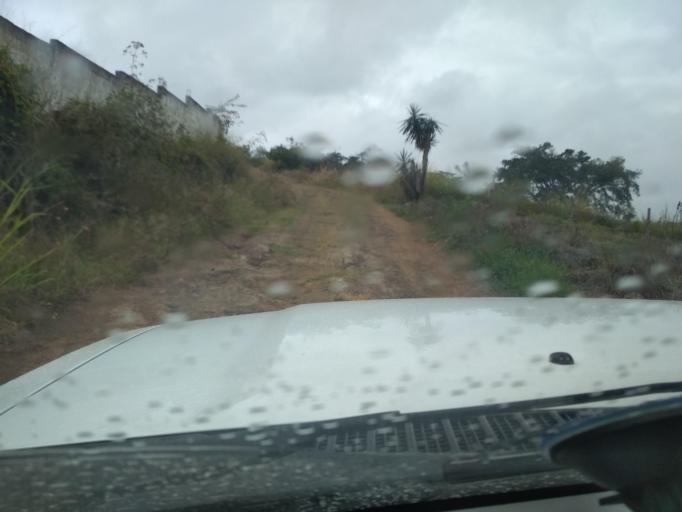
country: MX
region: Veracruz
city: El Castillo
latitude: 19.5354
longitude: -96.8233
